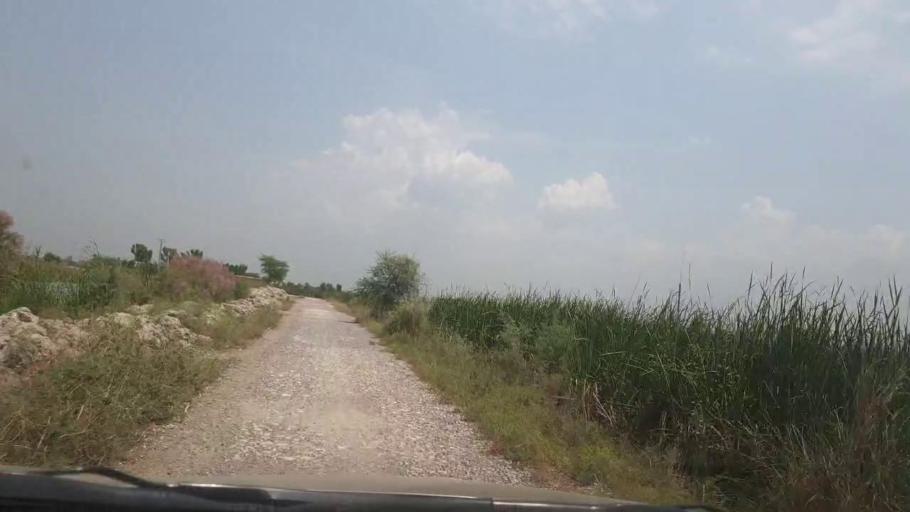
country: PK
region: Sindh
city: Naudero
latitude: 27.7221
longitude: 68.3288
